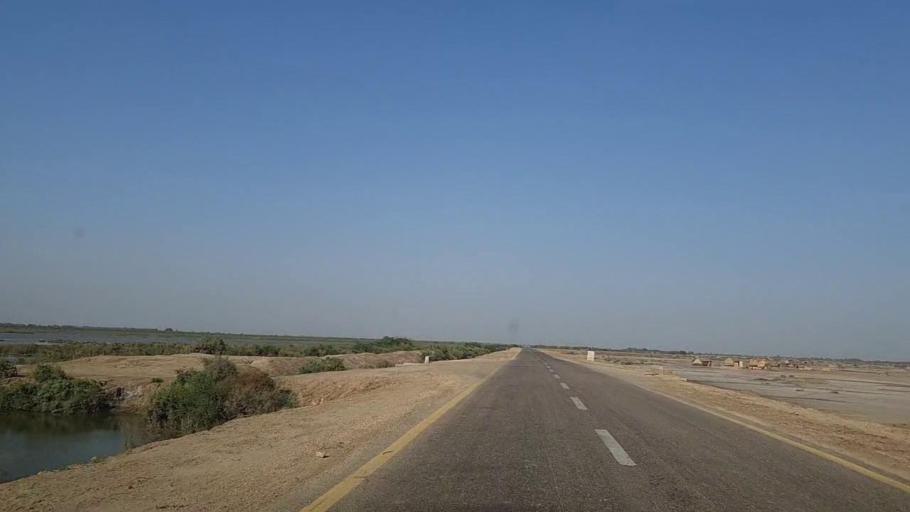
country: PK
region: Sindh
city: Jati
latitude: 24.4375
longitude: 68.3175
